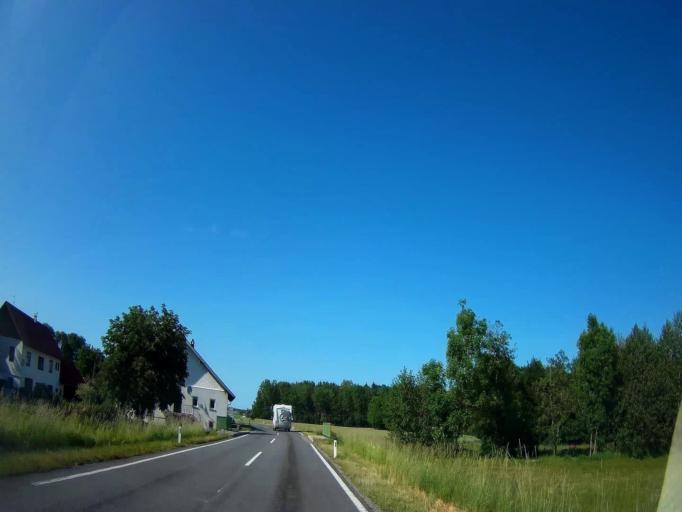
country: AT
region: Upper Austria
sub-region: Politischer Bezirk Braunau am Inn
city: Braunau am Inn
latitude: 48.1602
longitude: 13.0481
